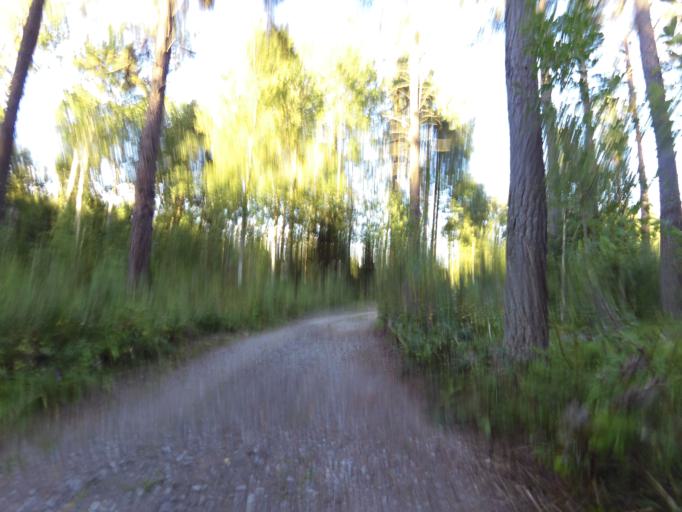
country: SE
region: Gaevleborg
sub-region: Gavle Kommun
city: Gavle
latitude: 60.7219
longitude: 17.1424
